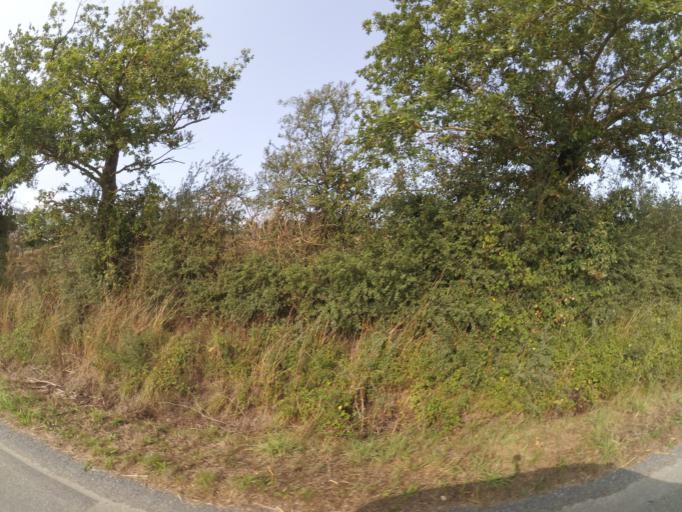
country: FR
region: Pays de la Loire
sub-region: Departement de la Vendee
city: La Bruffiere
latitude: 46.9934
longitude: -1.1917
